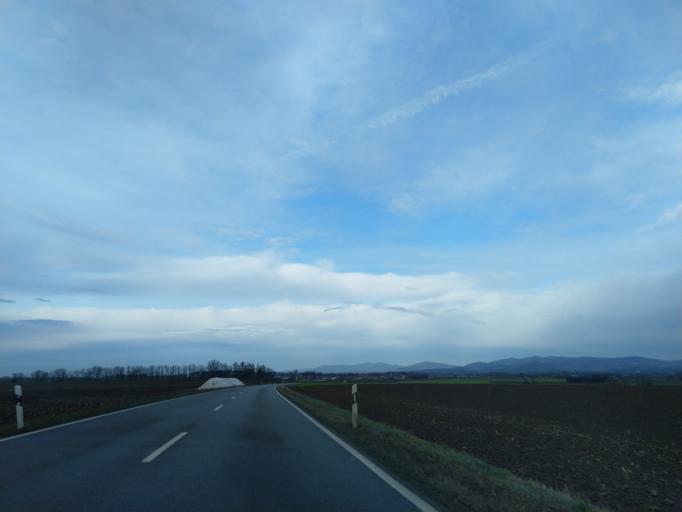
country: DE
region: Bavaria
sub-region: Lower Bavaria
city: Osterhofen
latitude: 48.6706
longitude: 13.0352
